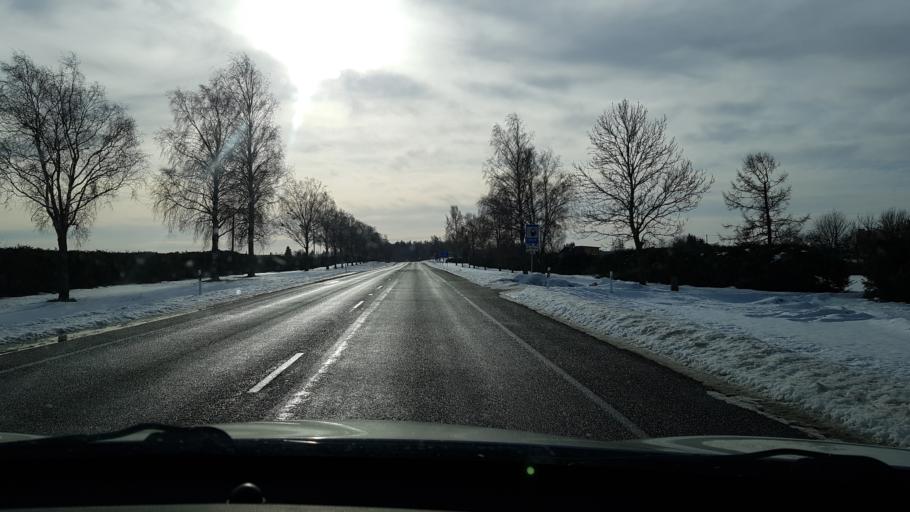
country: EE
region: Jaervamaa
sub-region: Paide linn
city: Paide
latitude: 58.9236
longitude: 25.6127
